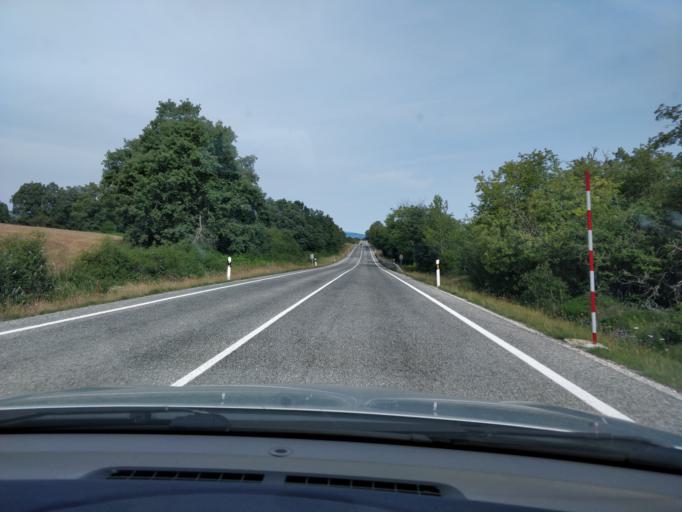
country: ES
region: Cantabria
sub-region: Provincia de Cantabria
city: San Martin de Elines
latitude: 42.9395
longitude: -3.7338
